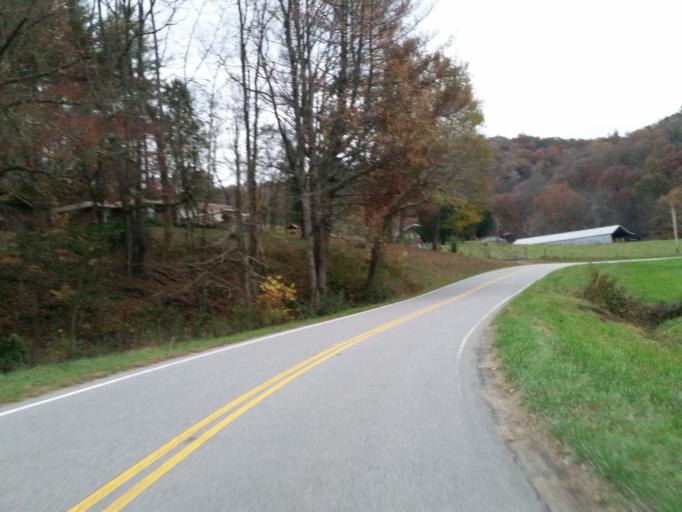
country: US
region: Georgia
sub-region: Union County
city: Blairsville
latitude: 34.7140
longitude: -84.0639
